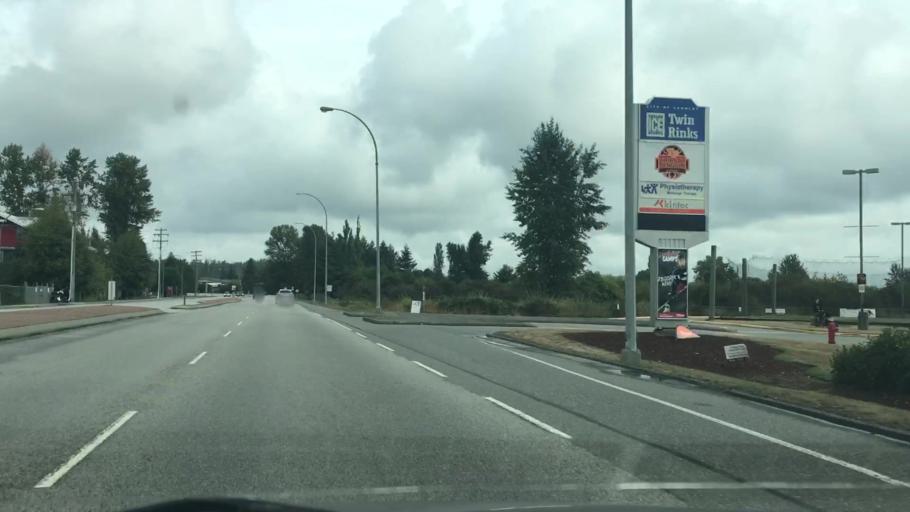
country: CA
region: British Columbia
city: Langley
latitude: 49.1061
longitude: -122.6428
